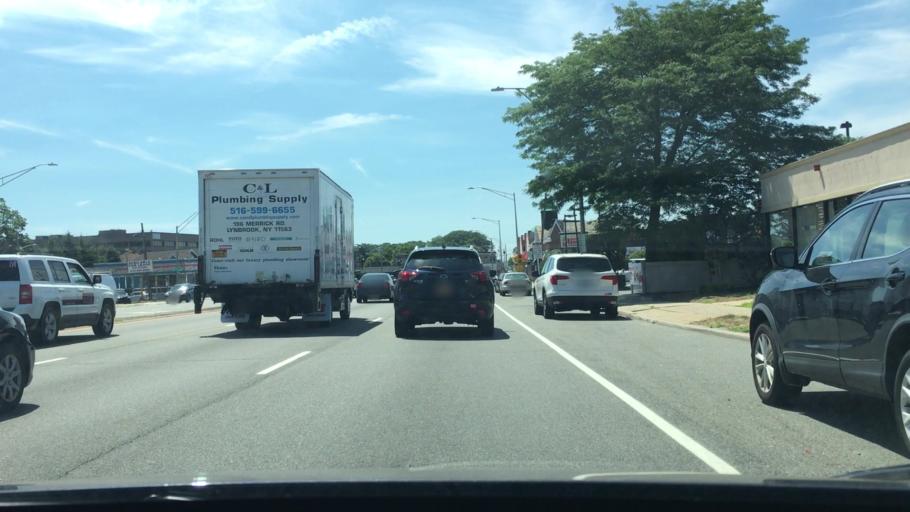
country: US
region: New York
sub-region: Nassau County
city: Wantagh
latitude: 40.6722
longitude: -73.5080
